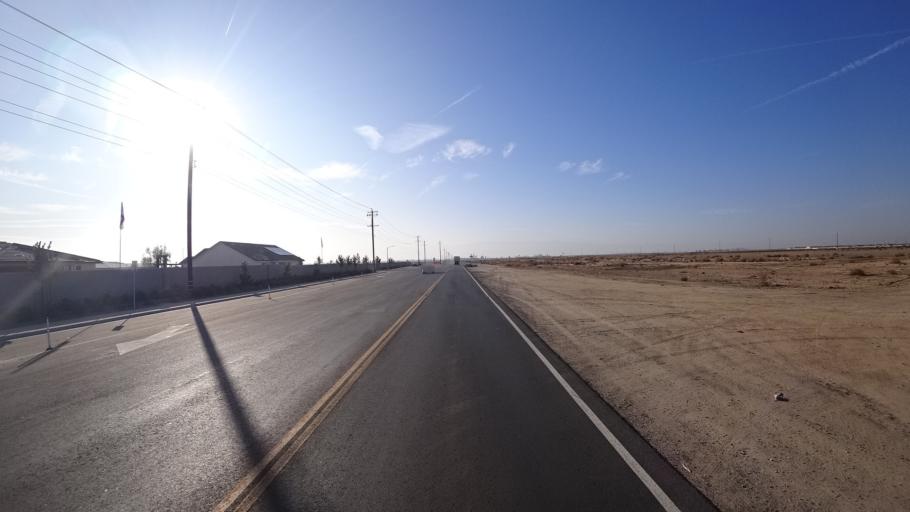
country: US
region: California
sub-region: Kern County
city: Greenacres
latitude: 35.2933
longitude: -119.0922
